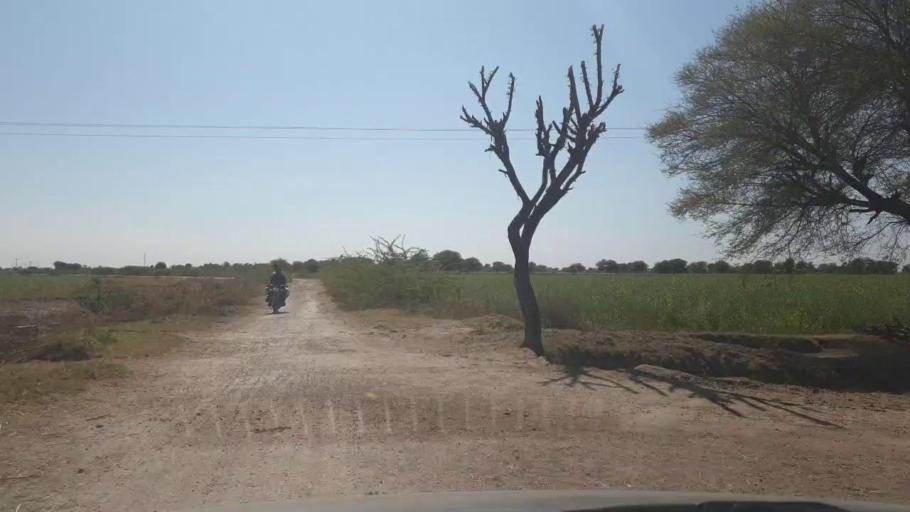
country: PK
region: Sindh
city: Dhoro Naro
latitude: 25.4249
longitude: 69.6202
